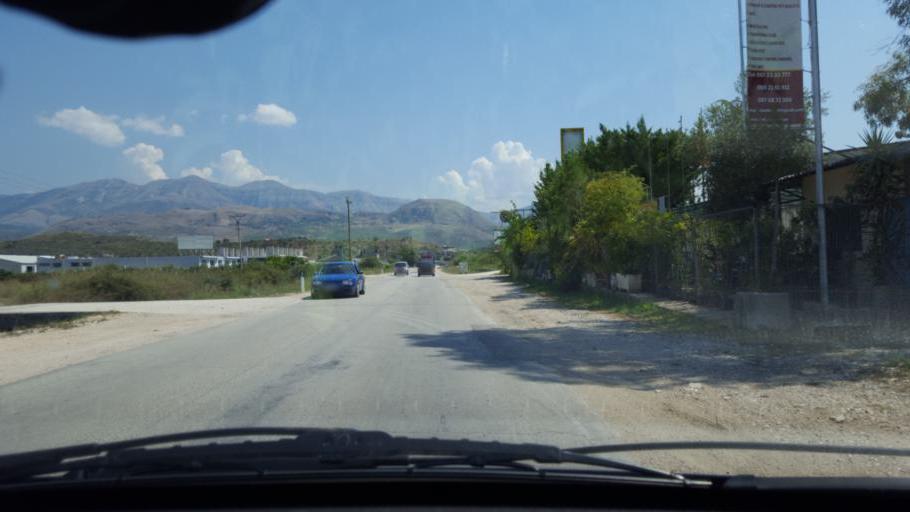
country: AL
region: Vlore
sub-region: Rrethi i Delvines
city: Finiq
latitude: 39.8936
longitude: 20.0689
